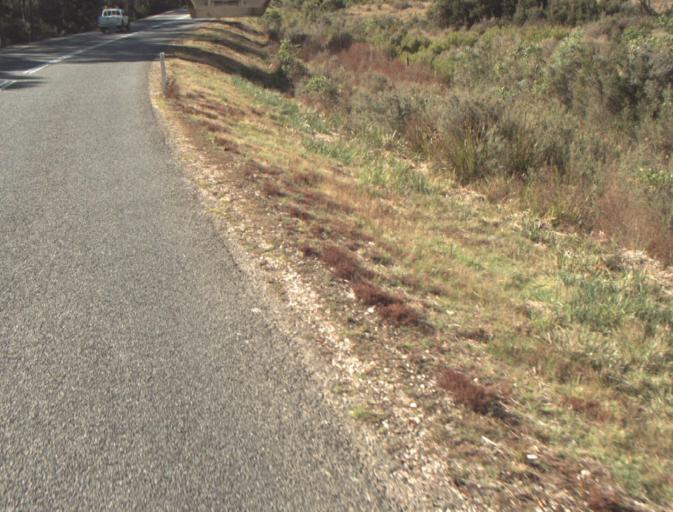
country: AU
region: Tasmania
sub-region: Launceston
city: Mayfield
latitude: -41.3310
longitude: 147.1796
